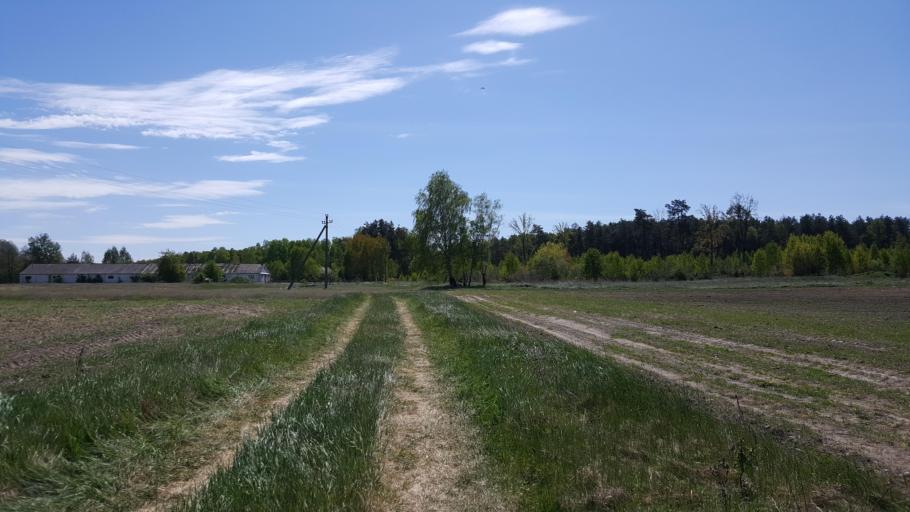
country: BY
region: Brest
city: Zhabinka
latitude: 52.3620
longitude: 24.0550
